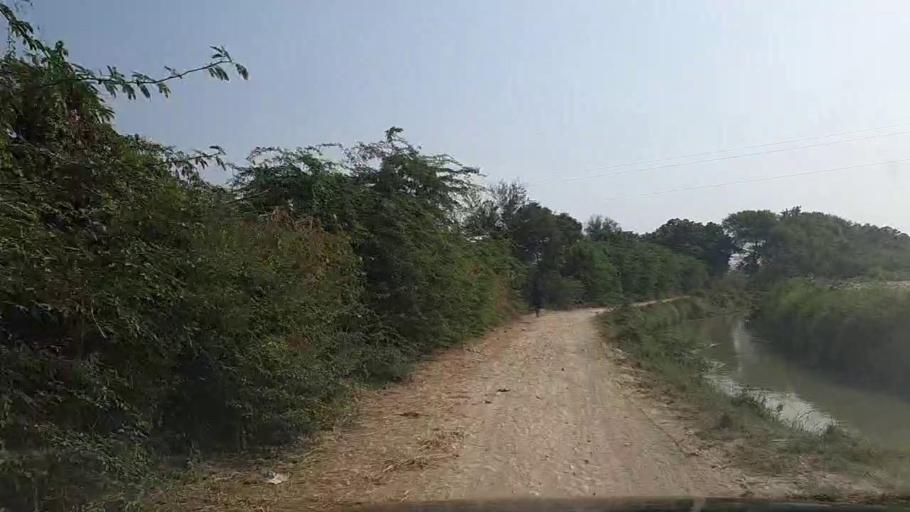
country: PK
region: Sindh
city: Mirpur Batoro
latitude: 24.7024
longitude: 68.2174
